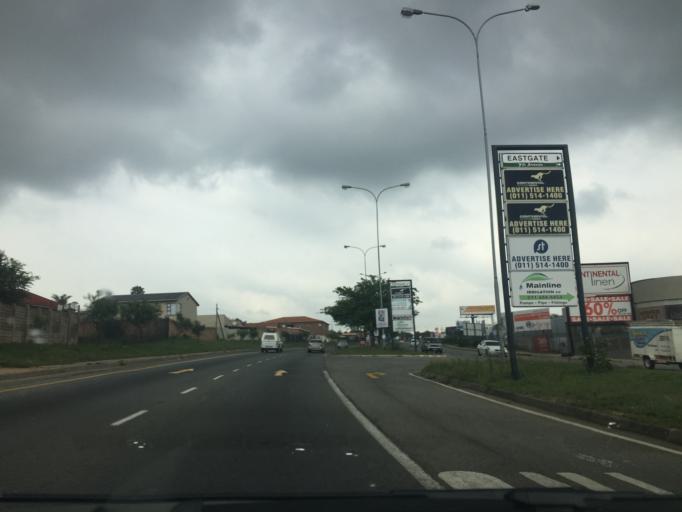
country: ZA
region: Gauteng
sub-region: City of Johannesburg Metropolitan Municipality
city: Modderfontein
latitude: -26.0890
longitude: 28.0957
